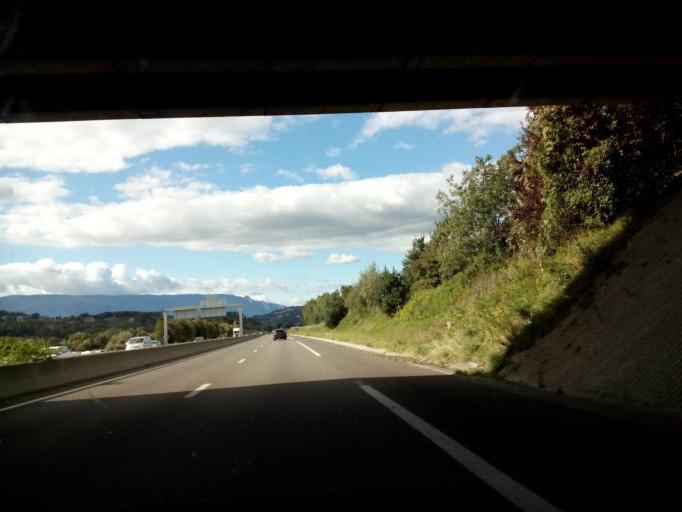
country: FR
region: Rhone-Alpes
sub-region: Departement de la Savoie
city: Saint-Baldoph
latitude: 45.5372
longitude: 5.9679
